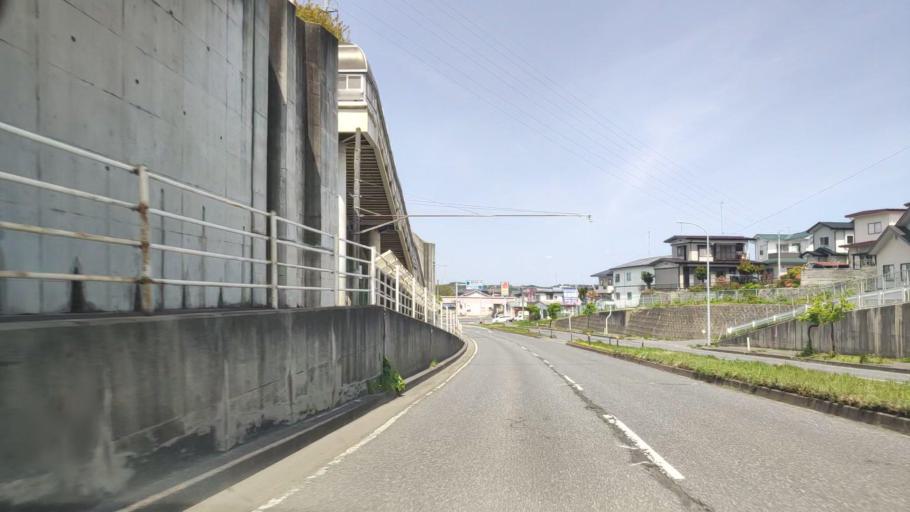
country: JP
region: Aomori
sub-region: Hachinohe Shi
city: Uchimaru
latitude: 40.5004
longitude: 141.4557
